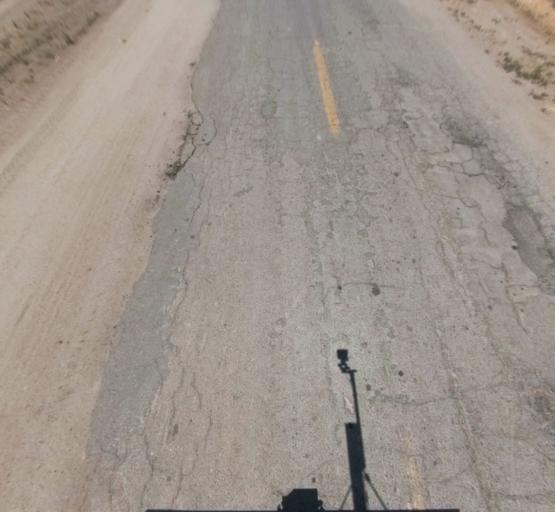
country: US
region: California
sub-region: Madera County
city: Chowchilla
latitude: 37.0906
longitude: -120.3335
